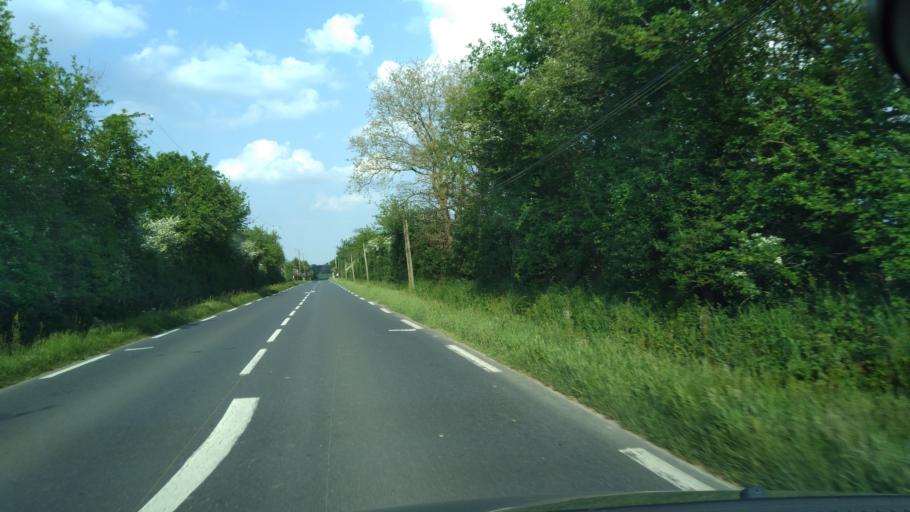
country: FR
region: Pays de la Loire
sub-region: Departement de la Loire-Atlantique
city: Heric
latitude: 47.4251
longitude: -1.6215
